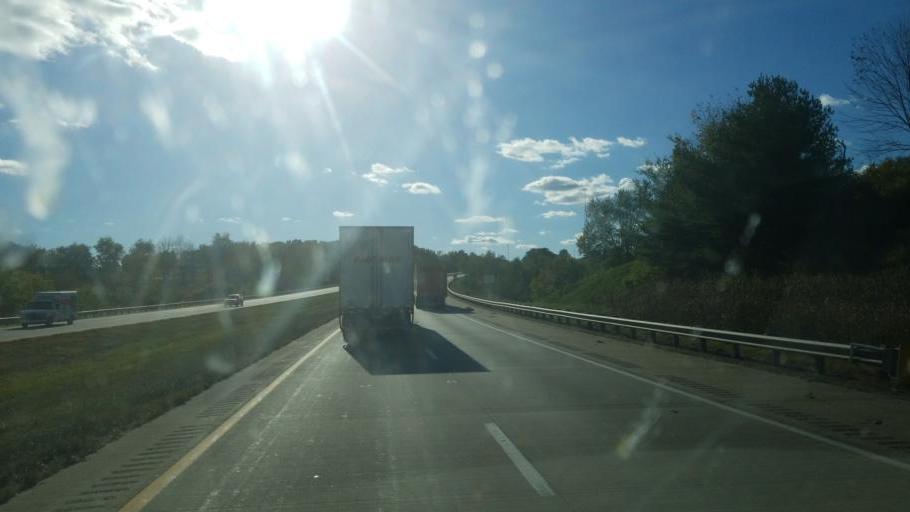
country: US
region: Ohio
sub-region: Belmont County
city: Bethesda
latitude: 40.0572
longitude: -81.0615
